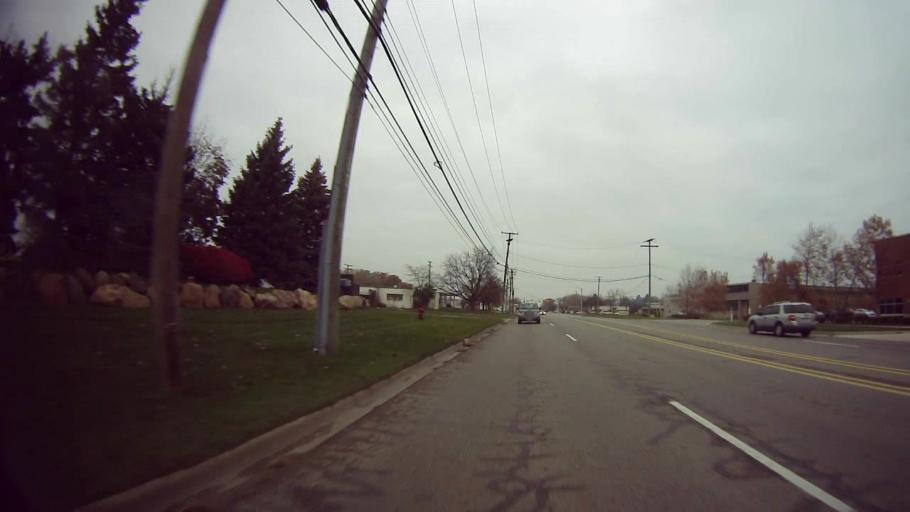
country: US
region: Michigan
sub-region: Oakland County
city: Clawson
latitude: 42.5473
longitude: -83.1326
